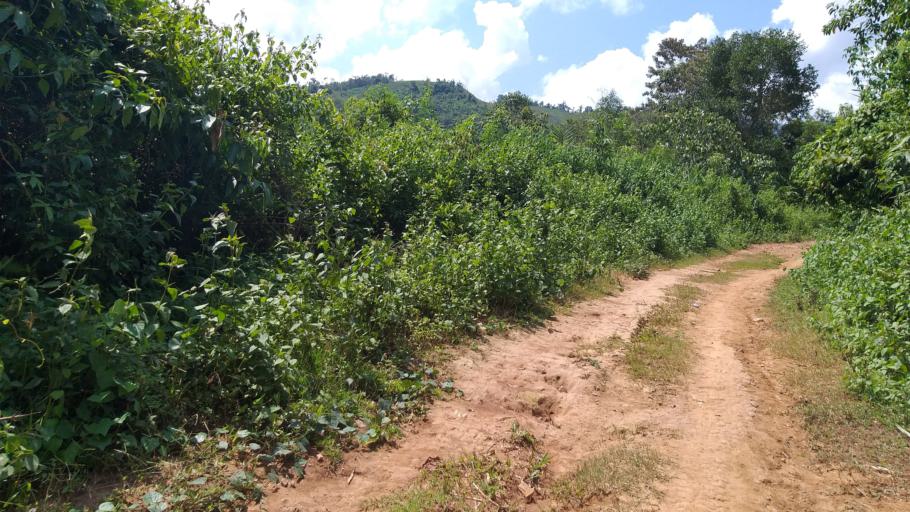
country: LA
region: Phongsali
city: Khoa
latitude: 21.3708
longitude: 102.5292
